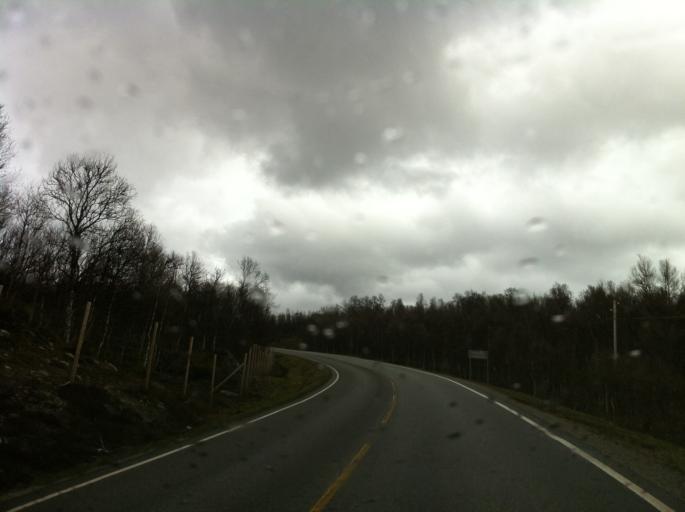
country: NO
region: Sor-Trondelag
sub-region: Tydal
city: Aas
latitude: 62.6467
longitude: 11.8744
